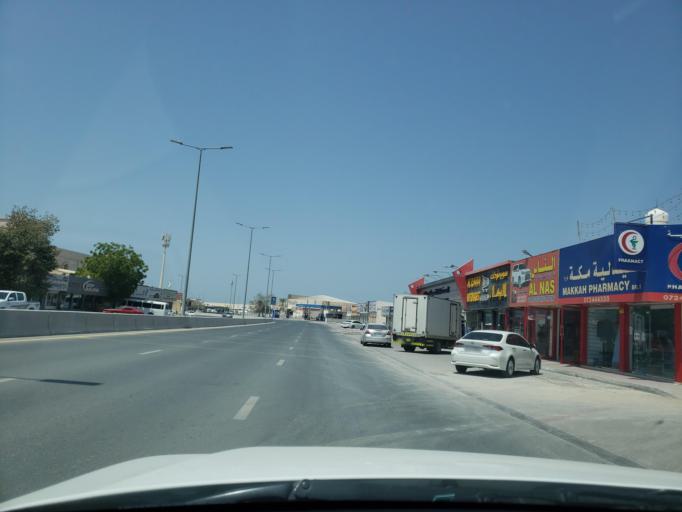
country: AE
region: Ra's al Khaymah
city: Ras al-Khaimah
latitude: 25.8162
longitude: 55.9713
